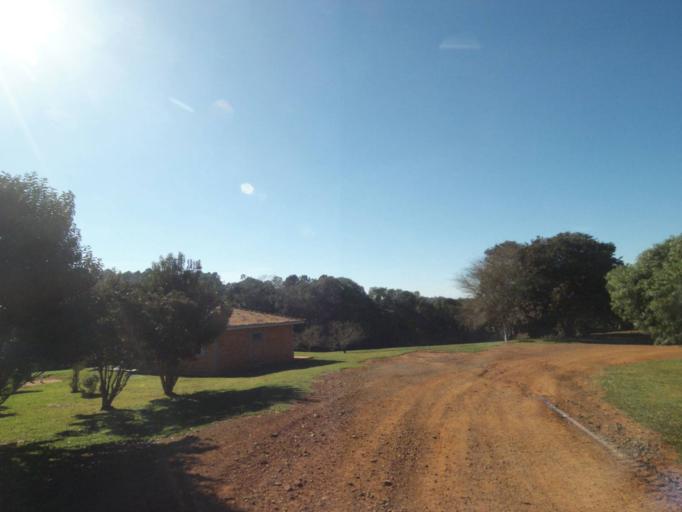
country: BR
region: Parana
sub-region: Tibagi
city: Tibagi
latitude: -24.3889
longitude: -50.3264
